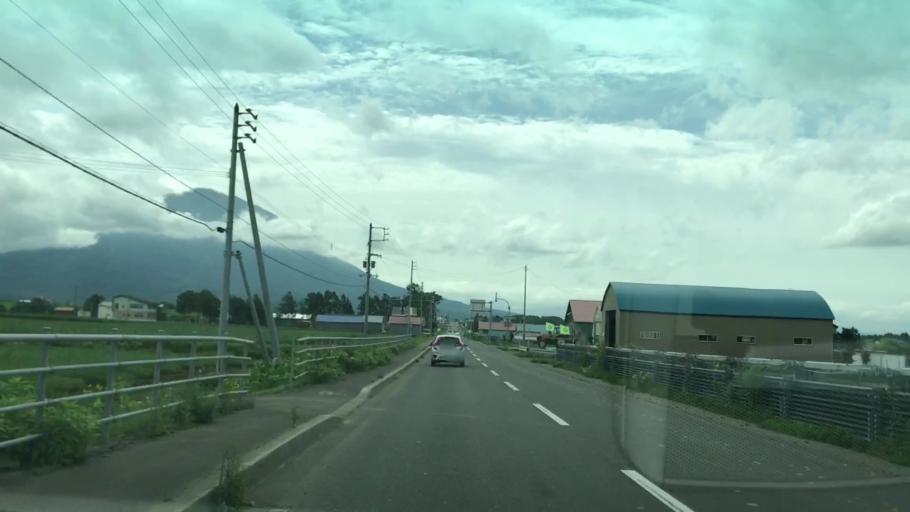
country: JP
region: Hokkaido
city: Niseko Town
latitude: 42.9319
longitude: 140.7759
